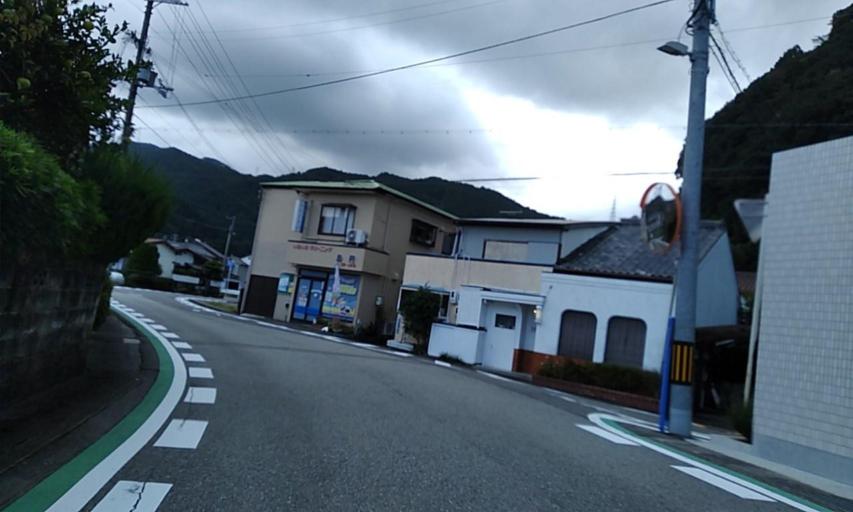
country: JP
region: Wakayama
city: Shingu
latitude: 33.7219
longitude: 135.9845
